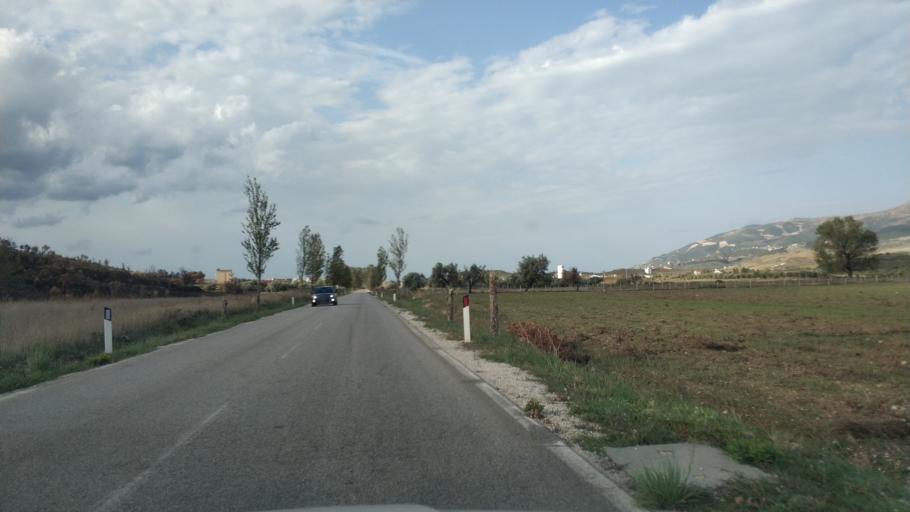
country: AL
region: Vlore
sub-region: Rrethi i Vlores
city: Orikum
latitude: 40.3168
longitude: 19.4842
